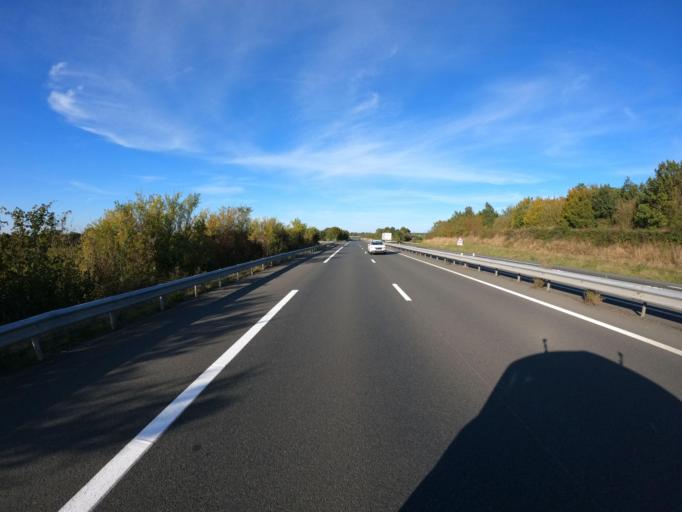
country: FR
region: Pays de la Loire
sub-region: Departement de Maine-et-Loire
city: Saint-Lambert-du-Lattay
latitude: 47.2924
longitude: -0.6133
